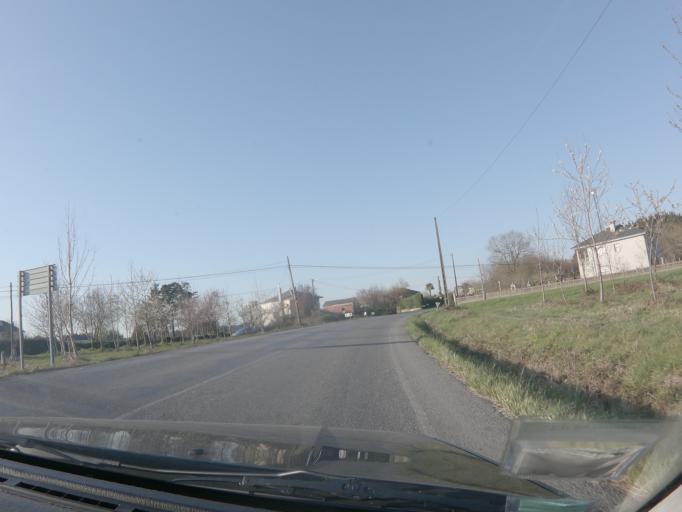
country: ES
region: Galicia
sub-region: Provincia de Lugo
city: Corgo
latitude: 42.9362
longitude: -7.3990
